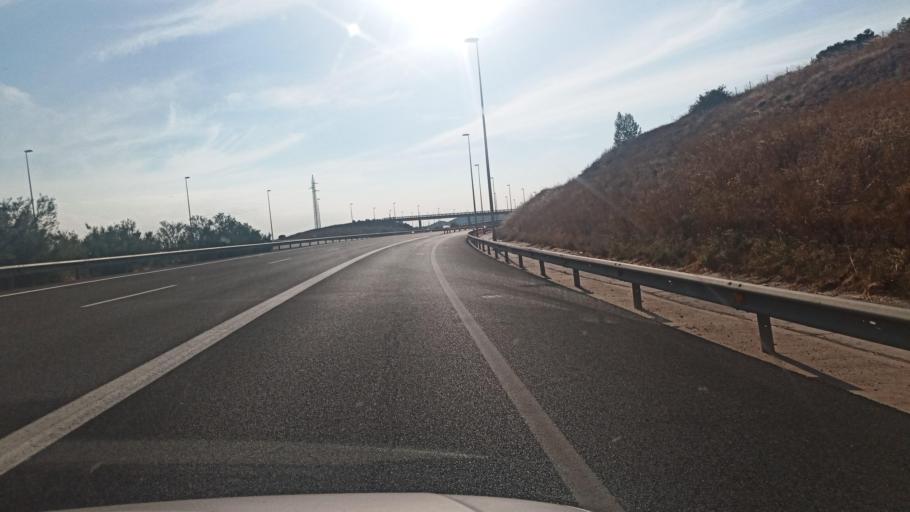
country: ES
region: Castille and Leon
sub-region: Provincia de Burgos
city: Hurones
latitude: 42.3716
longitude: -3.6248
